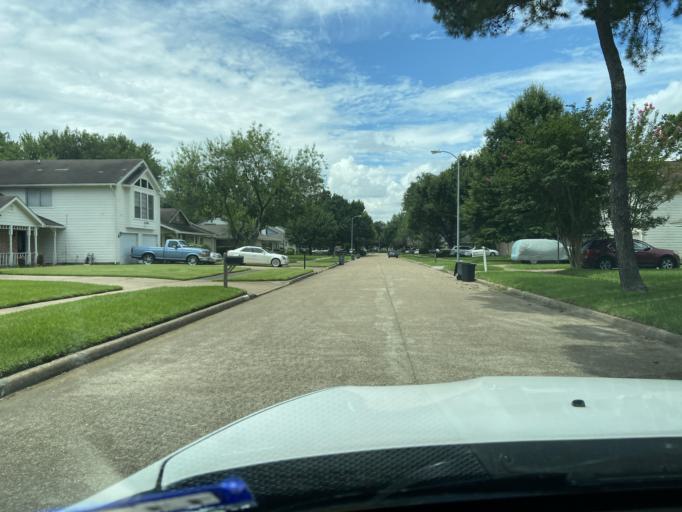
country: US
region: Texas
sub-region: Harris County
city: Jersey Village
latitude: 29.9150
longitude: -95.5746
